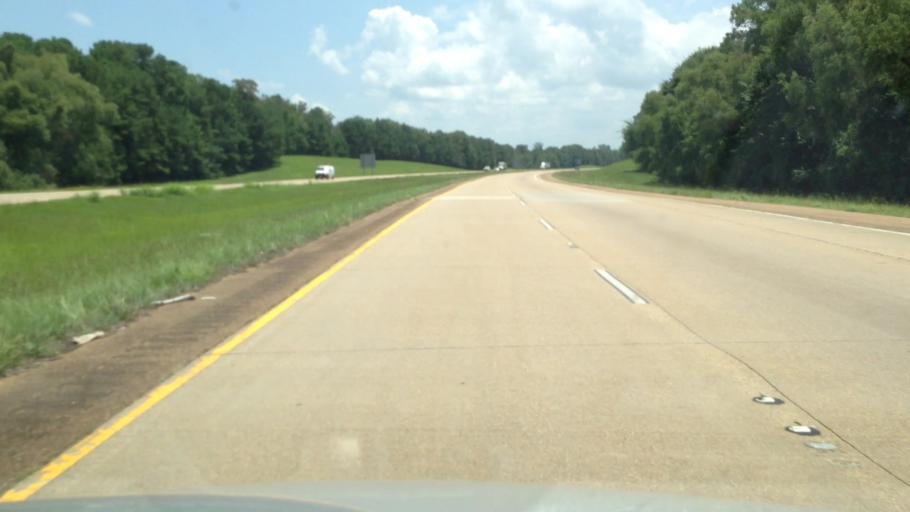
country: US
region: Louisiana
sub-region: Rapides Parish
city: Woodworth
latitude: 31.1573
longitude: -92.4559
